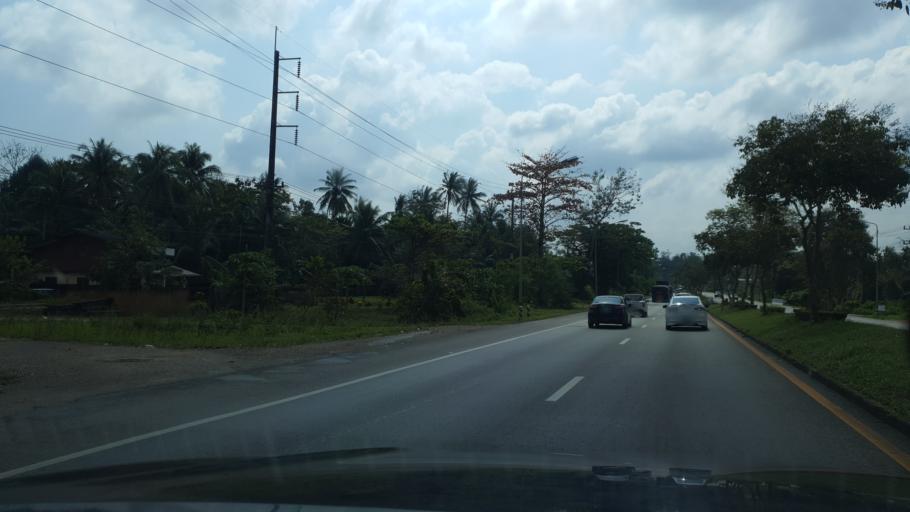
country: TH
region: Chumphon
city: Chumphon
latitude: 10.5579
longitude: 99.1164
